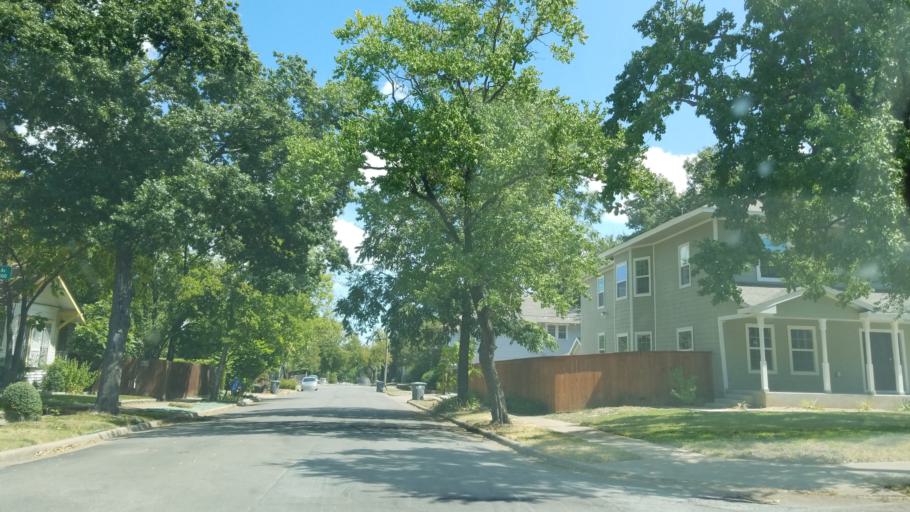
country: US
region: Texas
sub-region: Dallas County
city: Dallas
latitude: 32.7538
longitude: -96.8304
